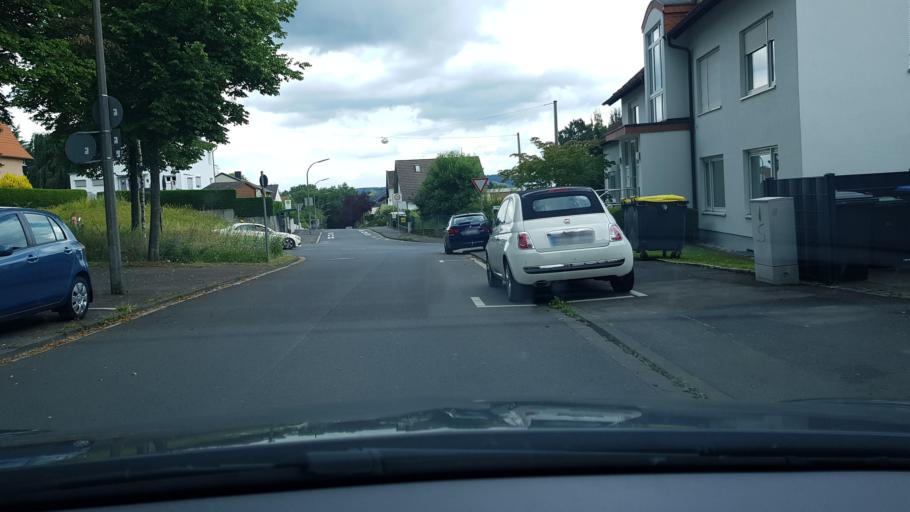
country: DE
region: North Rhine-Westphalia
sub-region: Regierungsbezirk Koln
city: Konigswinter
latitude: 50.6832
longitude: 7.1441
